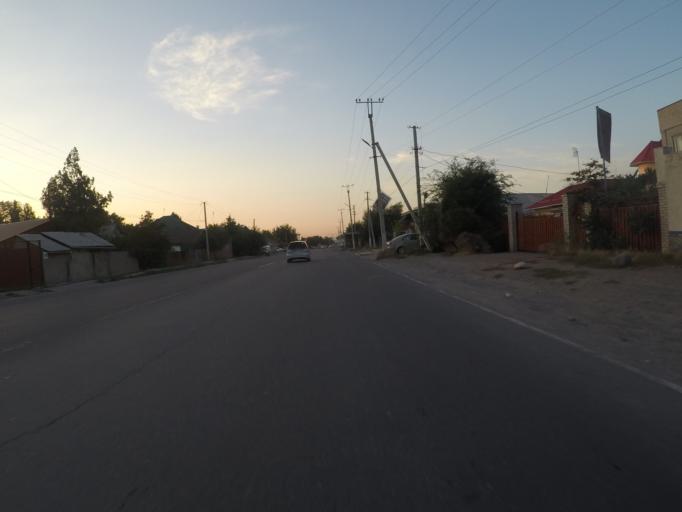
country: KG
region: Chuy
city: Lebedinovka
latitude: 42.8101
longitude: 74.6463
